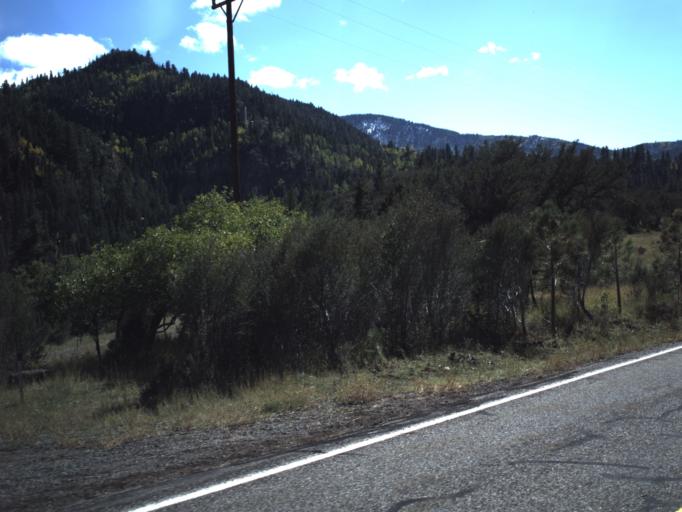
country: US
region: Utah
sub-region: Beaver County
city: Beaver
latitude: 38.2724
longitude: -112.4685
